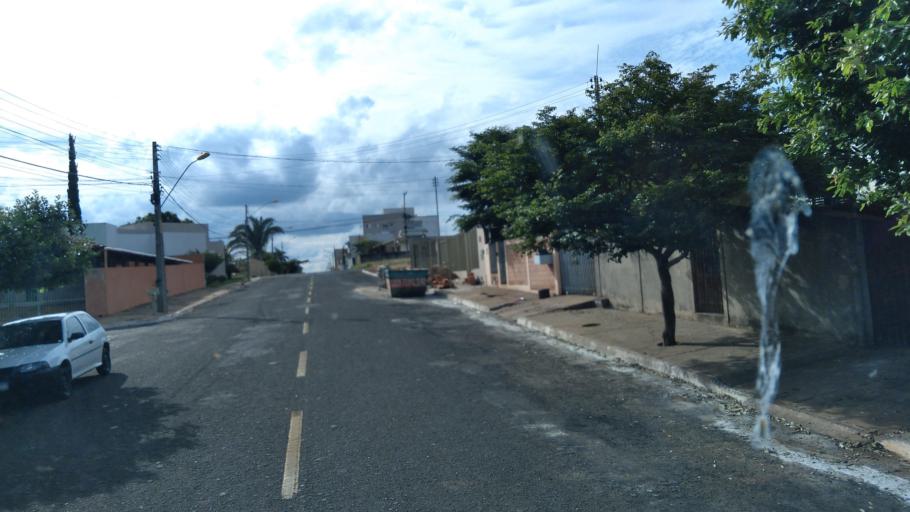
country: BR
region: Goias
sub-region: Mineiros
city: Mineiros
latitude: -17.5616
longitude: -52.5639
